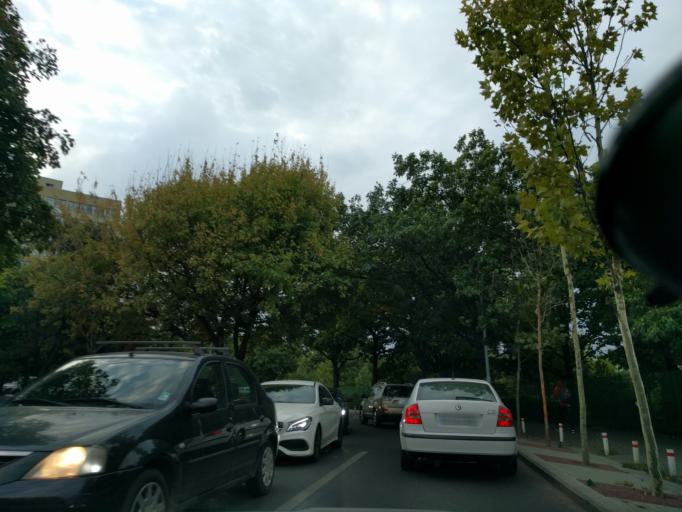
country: RO
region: Ilfov
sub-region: Comuna Fundeni-Dobroesti
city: Fundeni
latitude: 44.4240
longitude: 26.1569
